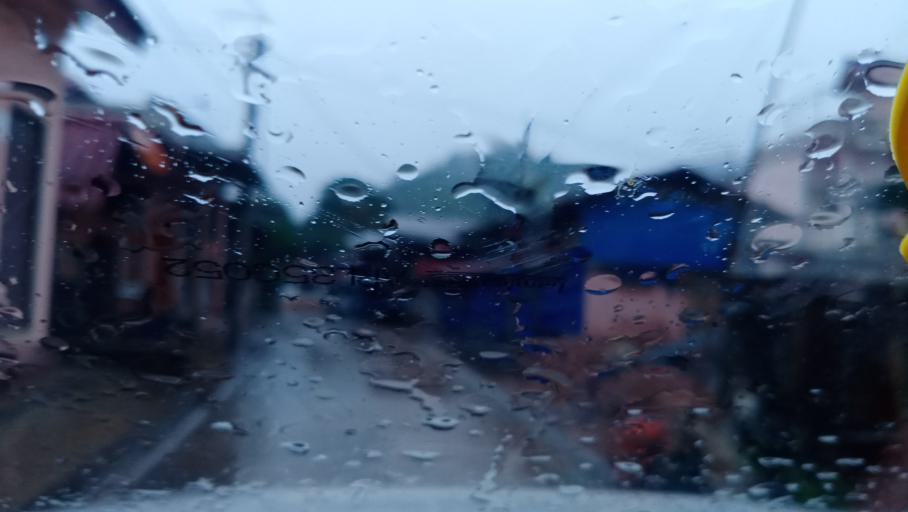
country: LA
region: Phongsali
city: Khoa
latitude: 21.0817
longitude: 102.5054
